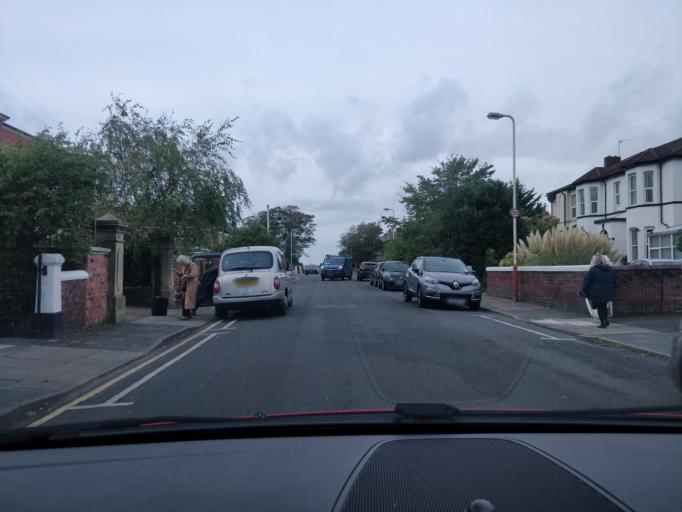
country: GB
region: England
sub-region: Sefton
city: Southport
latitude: 53.6544
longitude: -2.9989
